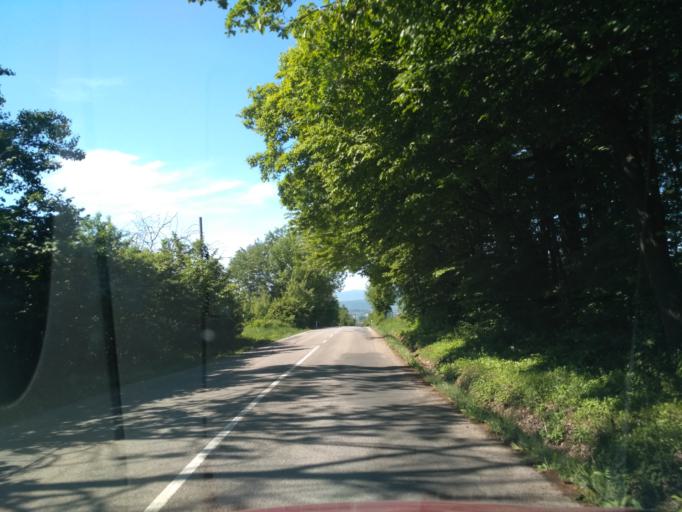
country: SK
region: Presovsky
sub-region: Okres Presov
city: Presov
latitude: 48.9429
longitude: 21.3006
